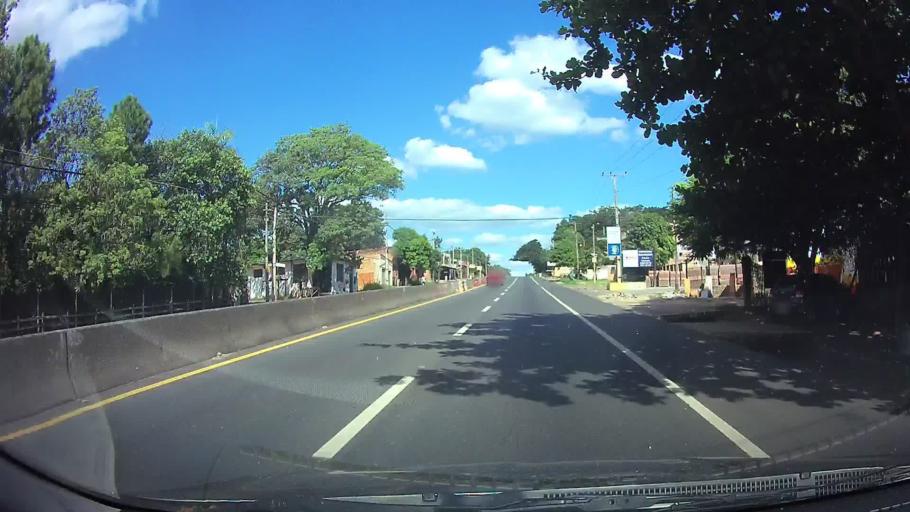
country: PY
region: Central
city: Itaugua
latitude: -25.3977
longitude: -57.3367
